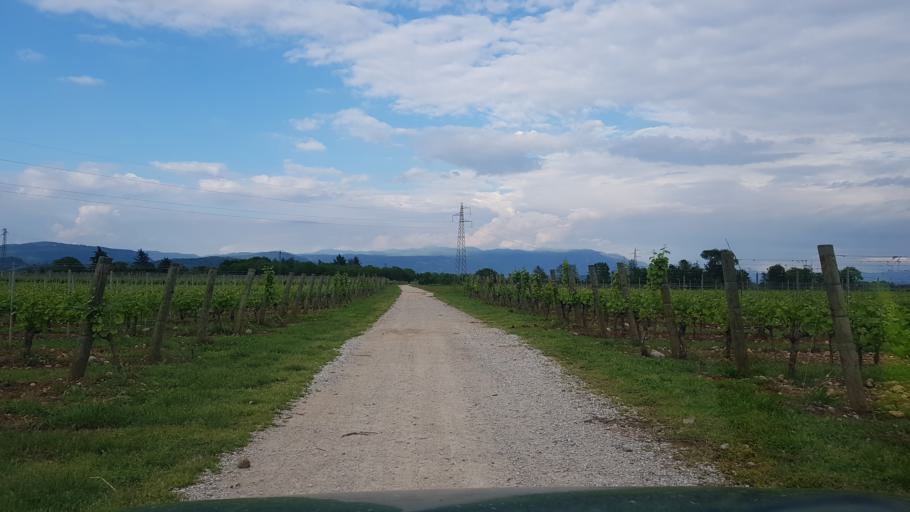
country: IT
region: Friuli Venezia Giulia
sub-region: Provincia di Gorizia
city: San Lorenzo Isontino
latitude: 45.9191
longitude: 13.5364
